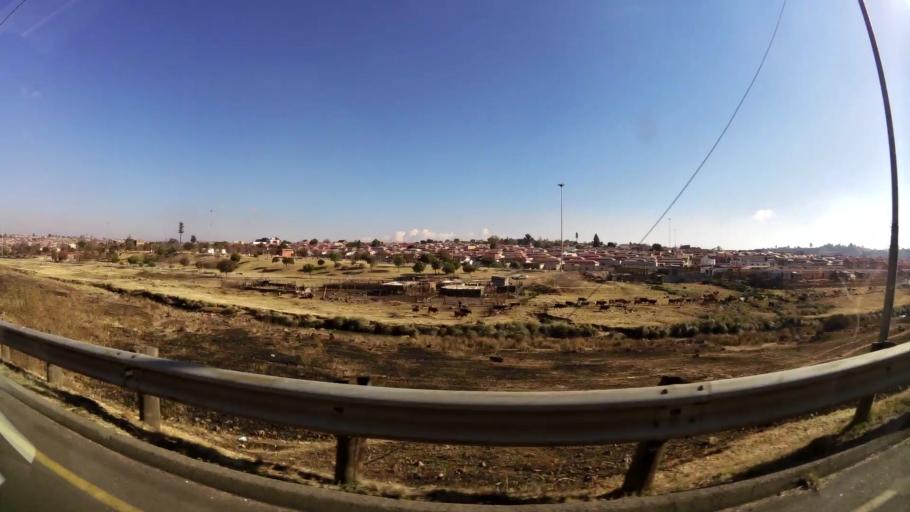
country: ZA
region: Gauteng
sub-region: City of Johannesburg Metropolitan Municipality
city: Soweto
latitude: -26.2286
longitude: 27.9233
